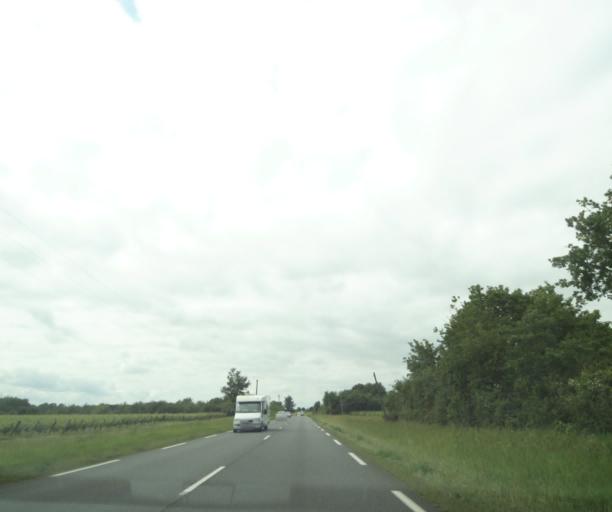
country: FR
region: Pays de la Loire
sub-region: Departement de Maine-et-Loire
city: Montreuil-Bellay
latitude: 47.1539
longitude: -0.1474
